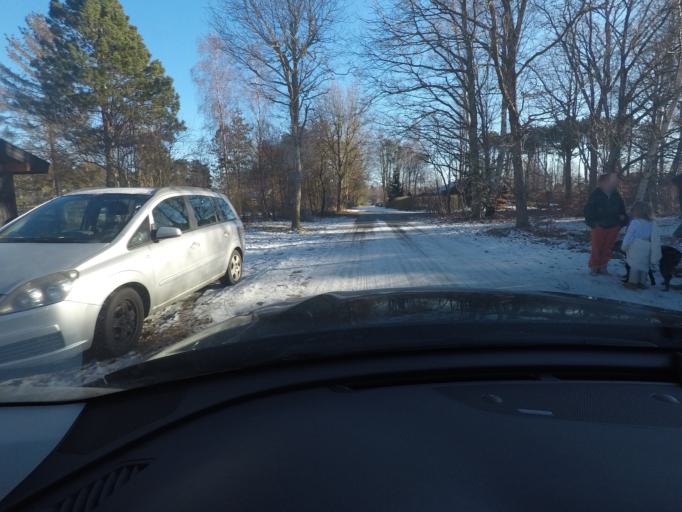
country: DK
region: Capital Region
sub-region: Halsnaes Kommune
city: Liseleje
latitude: 55.9963
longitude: 11.9426
